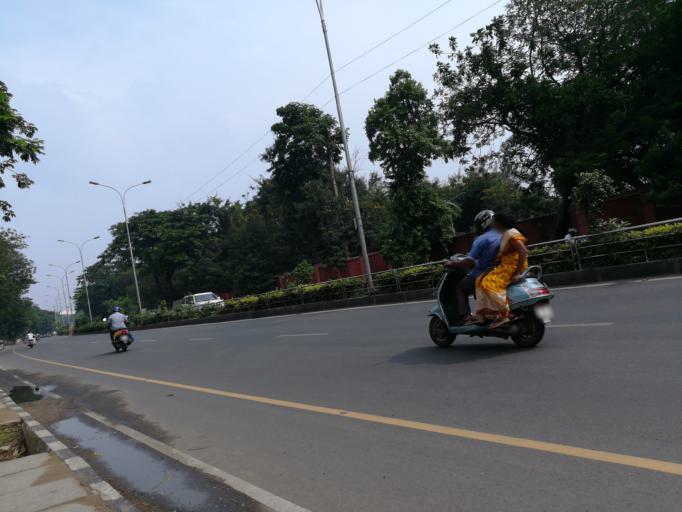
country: IN
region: Tamil Nadu
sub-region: Chennai
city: Gandhi Nagar
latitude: 13.0137
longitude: 80.2404
